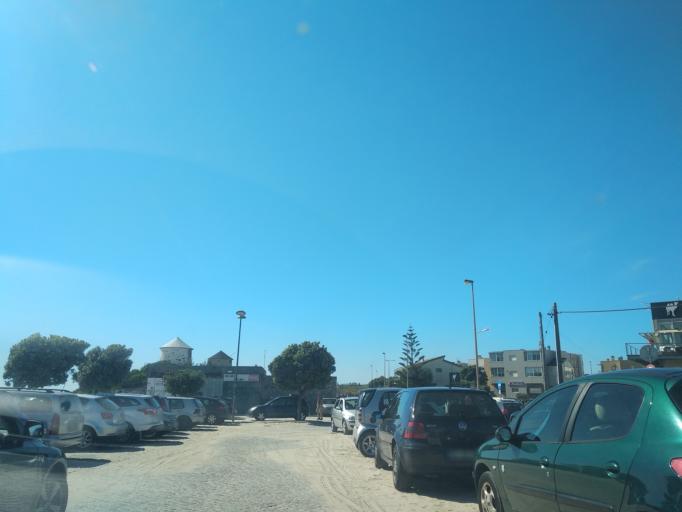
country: PT
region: Braga
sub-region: Esposende
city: Apulia
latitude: 41.4869
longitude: -8.7806
